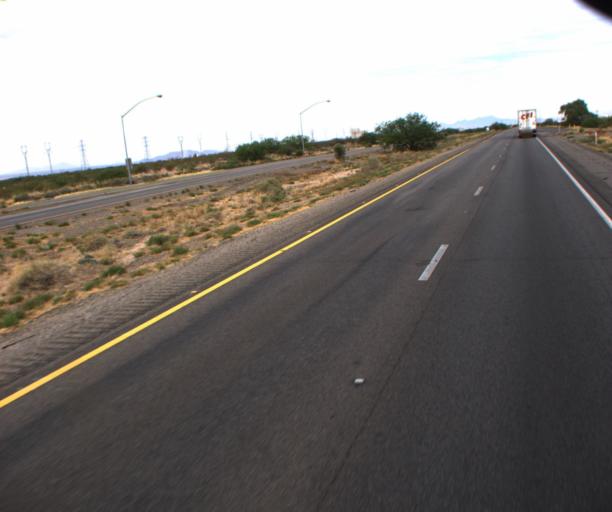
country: US
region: Arizona
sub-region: Pima County
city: Vail
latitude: 32.0630
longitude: -110.7757
